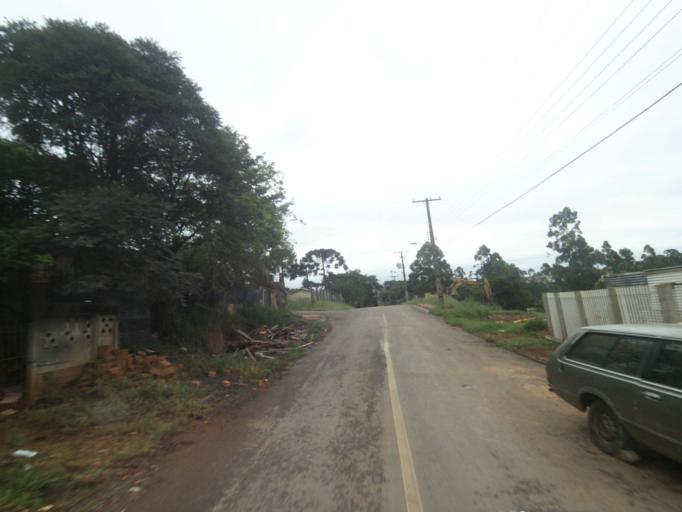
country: BR
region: Parana
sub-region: Telemaco Borba
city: Telemaco Borba
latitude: -24.3184
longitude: -50.6539
